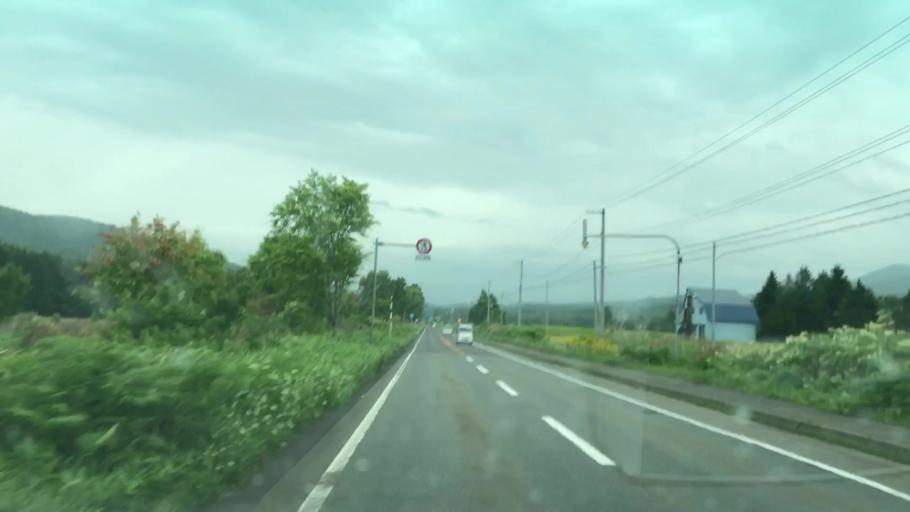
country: JP
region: Hokkaido
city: Niseko Town
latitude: 42.7653
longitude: 140.4826
